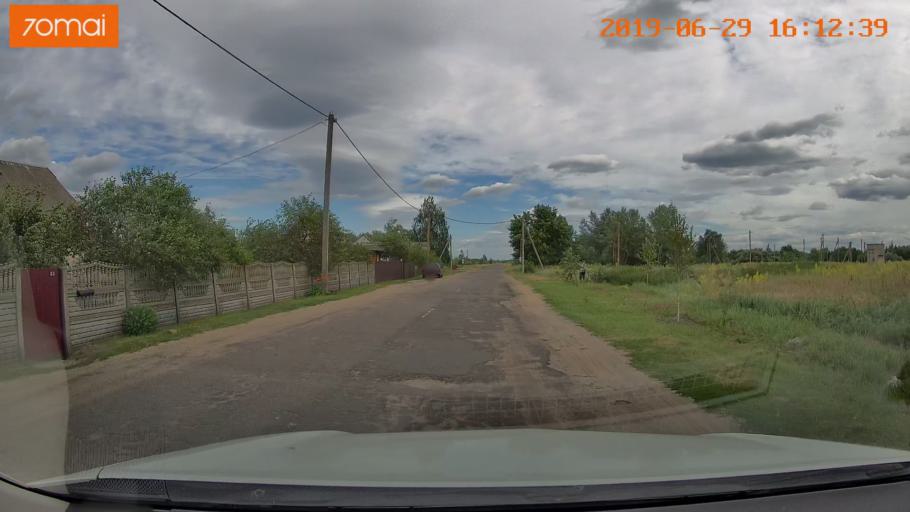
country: BY
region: Brest
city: Luninyets
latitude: 52.2001
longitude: 27.0156
